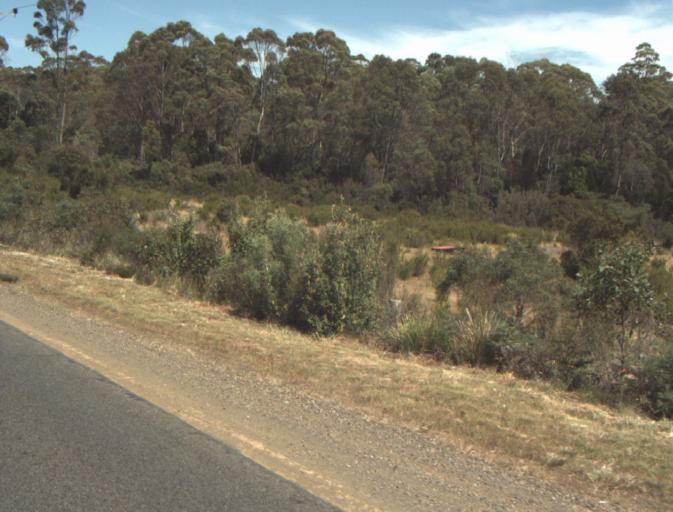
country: AU
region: Tasmania
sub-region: Launceston
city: Mayfield
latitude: -41.3034
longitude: 147.1334
